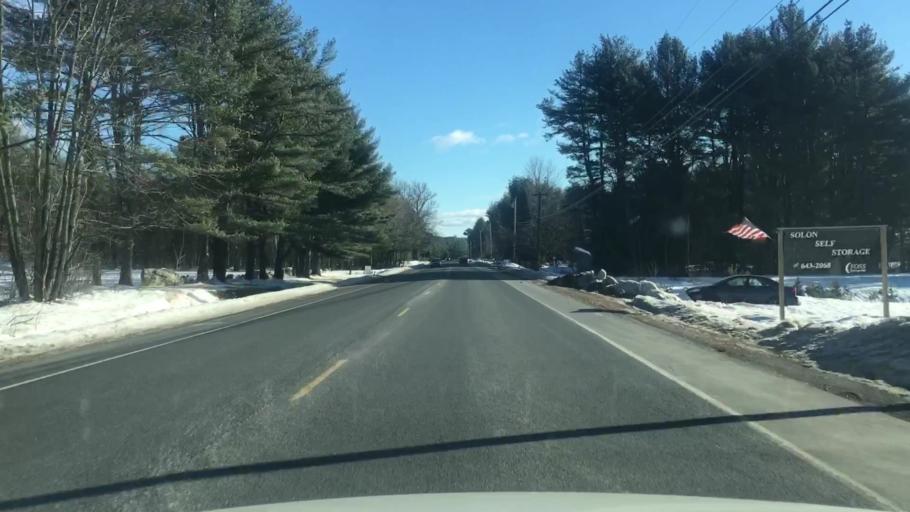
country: US
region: Maine
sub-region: Somerset County
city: Madison
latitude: 44.9421
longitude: -69.8483
